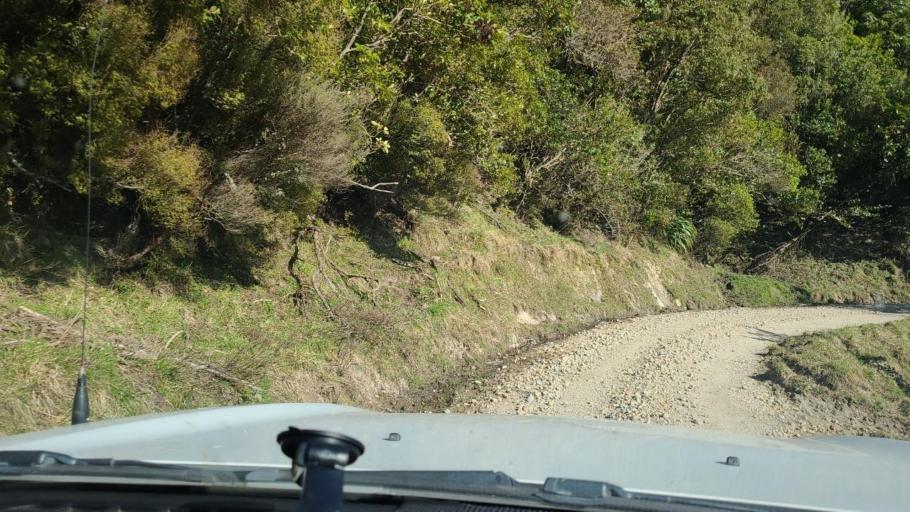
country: NZ
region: Hawke's Bay
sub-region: Wairoa District
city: Wairoa
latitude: -38.6832
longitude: 177.4588
